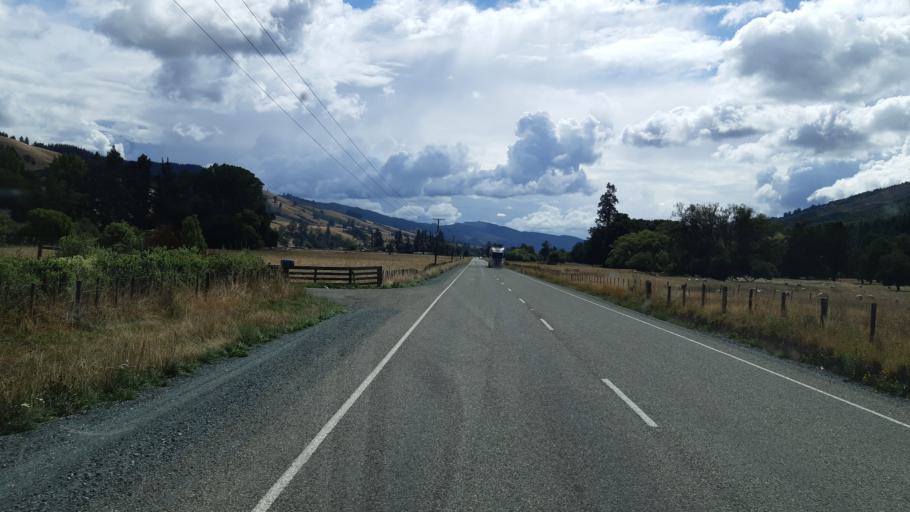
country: NZ
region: Tasman
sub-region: Tasman District
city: Wakefield
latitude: -41.5277
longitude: 172.7958
